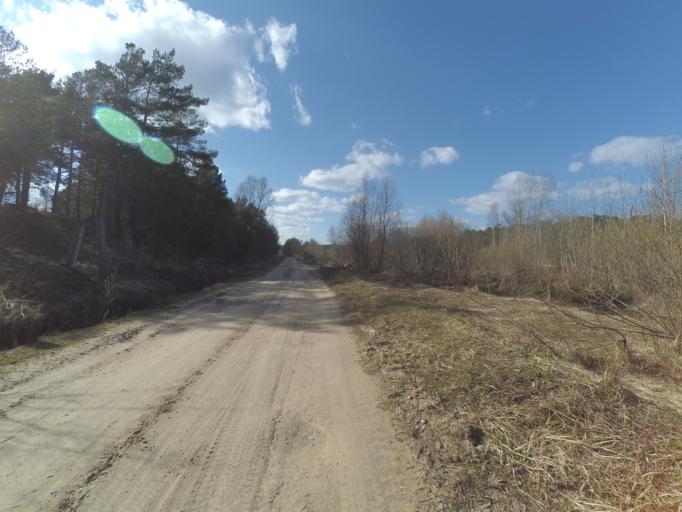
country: RU
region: Moskovskaya
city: Stupino
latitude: 54.8526
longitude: 37.9139
